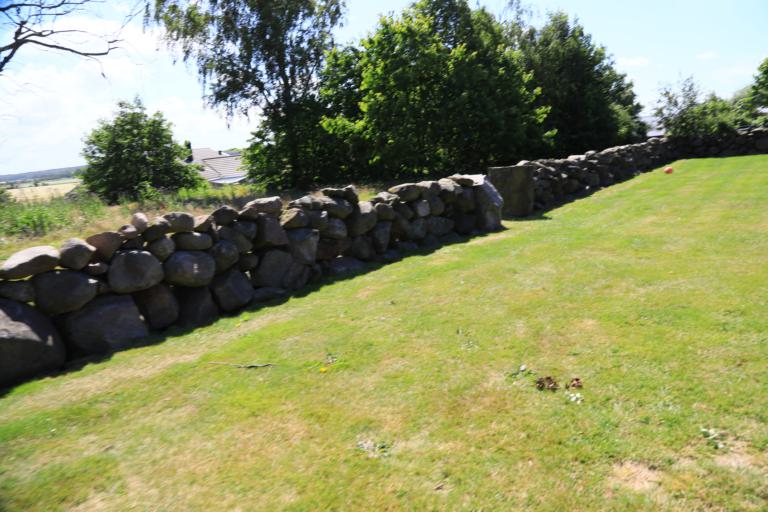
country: SE
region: Halland
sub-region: Varbergs Kommun
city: Traslovslage
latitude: 57.0990
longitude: 12.2971
